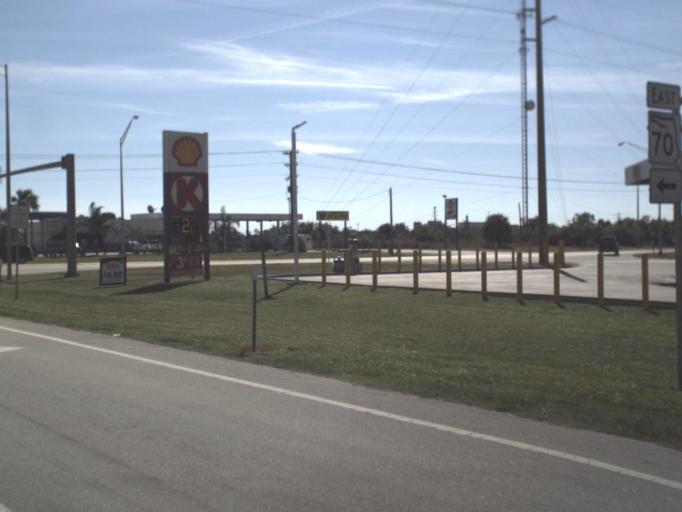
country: US
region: Florida
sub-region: Highlands County
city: Placid Lakes
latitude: 27.2091
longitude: -81.3288
